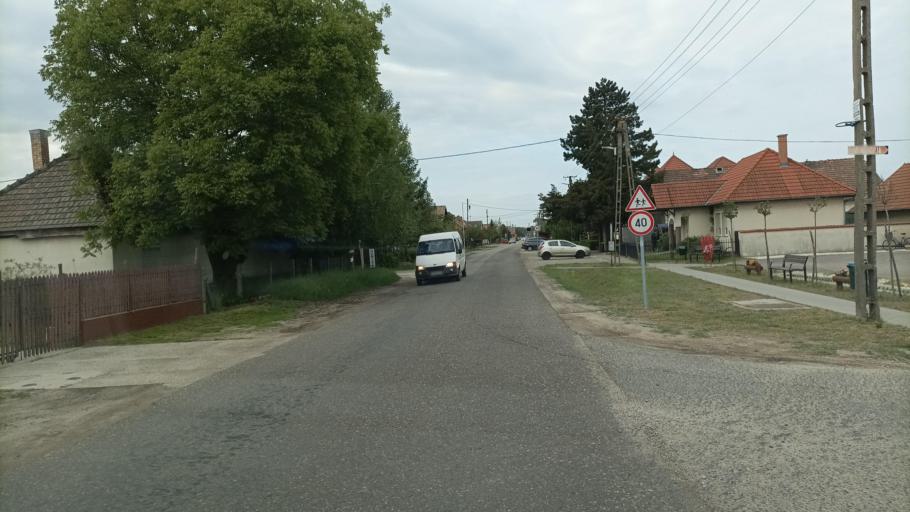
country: HU
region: Pest
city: Monor
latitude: 47.2980
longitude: 19.4300
